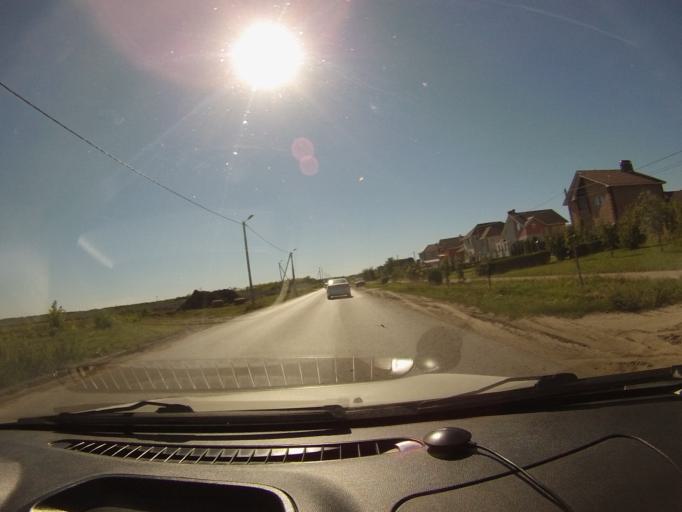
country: RU
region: Tambov
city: Tambov
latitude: 52.7660
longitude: 41.3867
